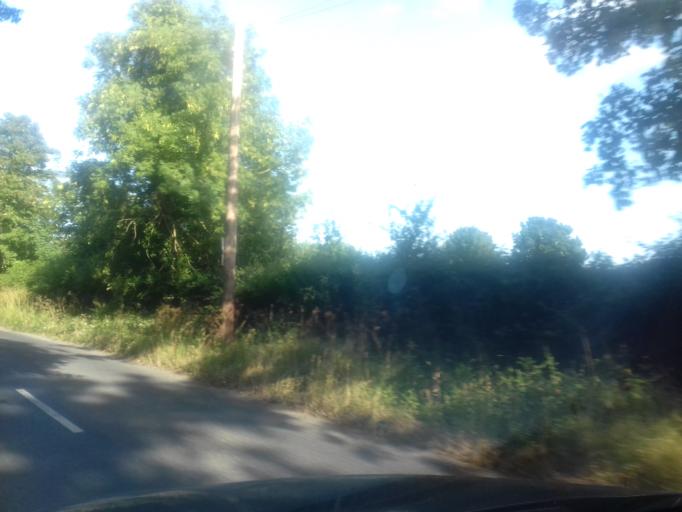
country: IE
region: Leinster
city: Hartstown
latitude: 53.4486
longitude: -6.4087
